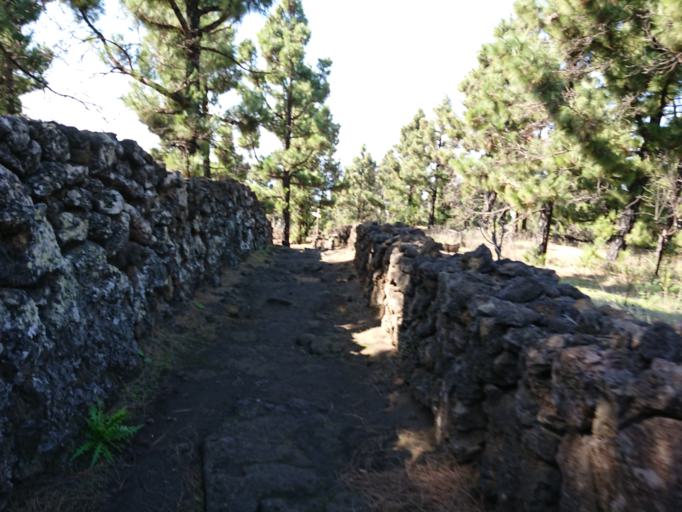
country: ES
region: Canary Islands
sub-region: Provincia de Santa Cruz de Tenerife
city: El Paso
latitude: 28.6062
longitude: -17.8684
